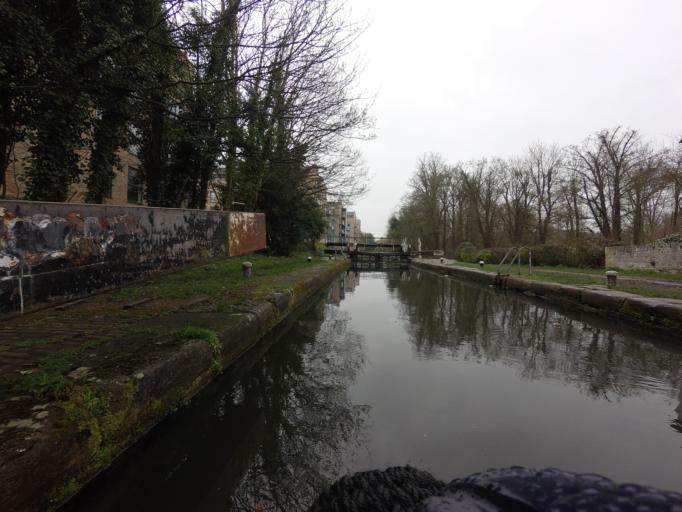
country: GB
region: England
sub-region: Hertfordshire
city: Kings Langley
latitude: 51.7300
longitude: -0.4539
